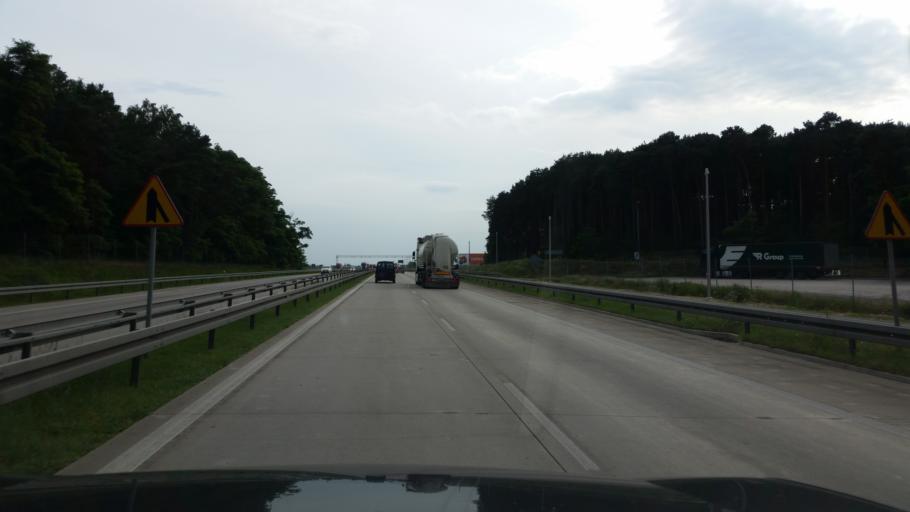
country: PL
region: Lodz Voivodeship
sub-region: Powiat piotrkowski
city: Wolborz
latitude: 51.4881
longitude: 19.8238
